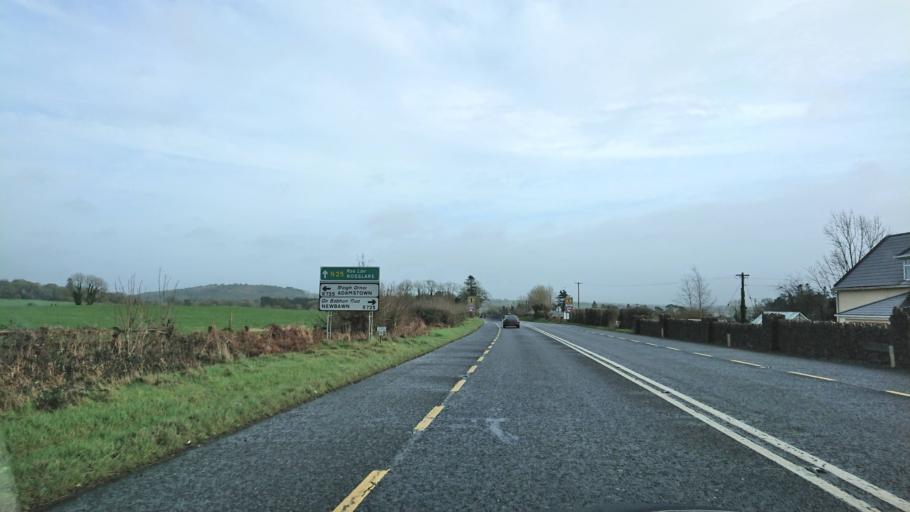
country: IE
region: Leinster
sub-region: Loch Garman
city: New Ross
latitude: 52.3620
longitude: -6.7638
